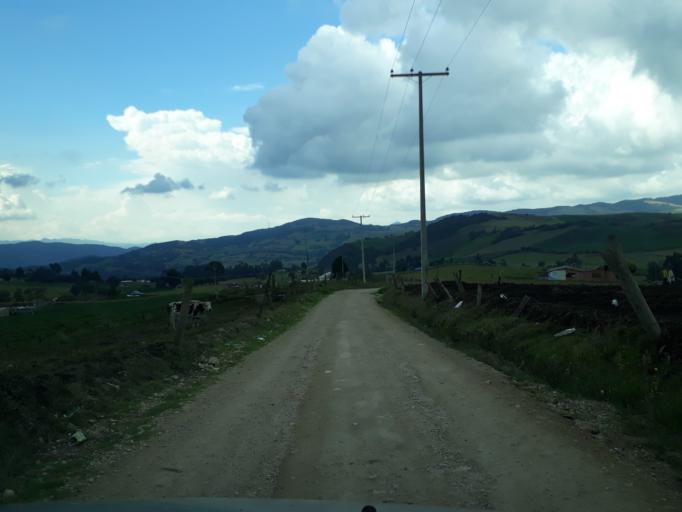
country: CO
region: Cundinamarca
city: Lenguazaque
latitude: 5.2456
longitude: -73.6765
